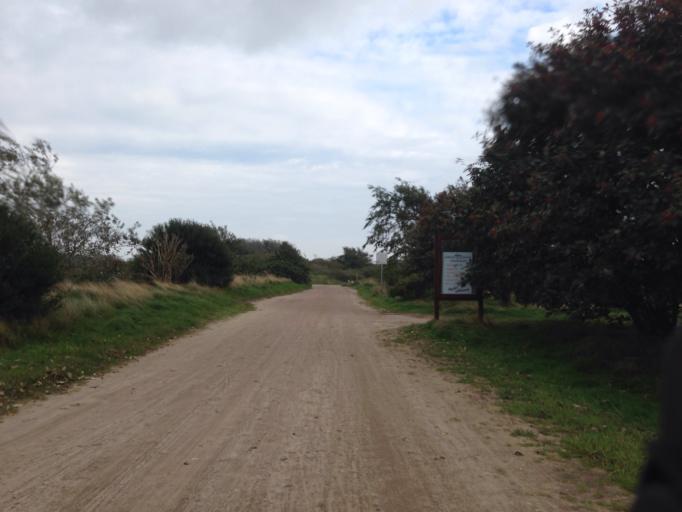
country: DE
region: Schleswig-Holstein
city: Nieblum
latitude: 54.6821
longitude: 8.4836
